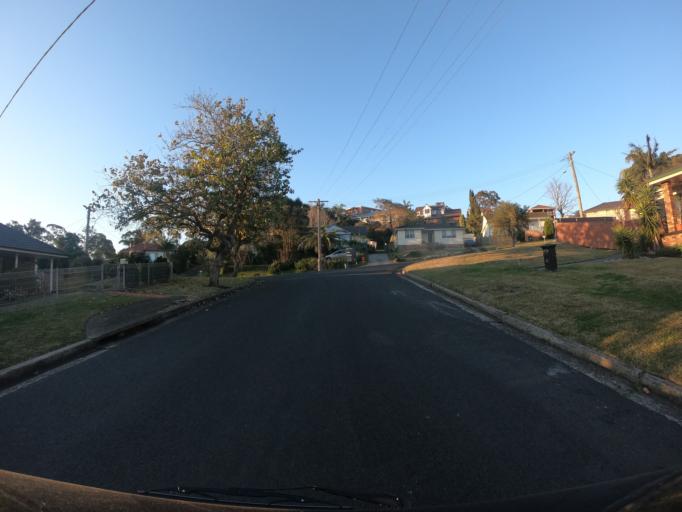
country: AU
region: New South Wales
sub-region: Wollongong
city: Berkeley
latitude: -34.4796
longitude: 150.8576
